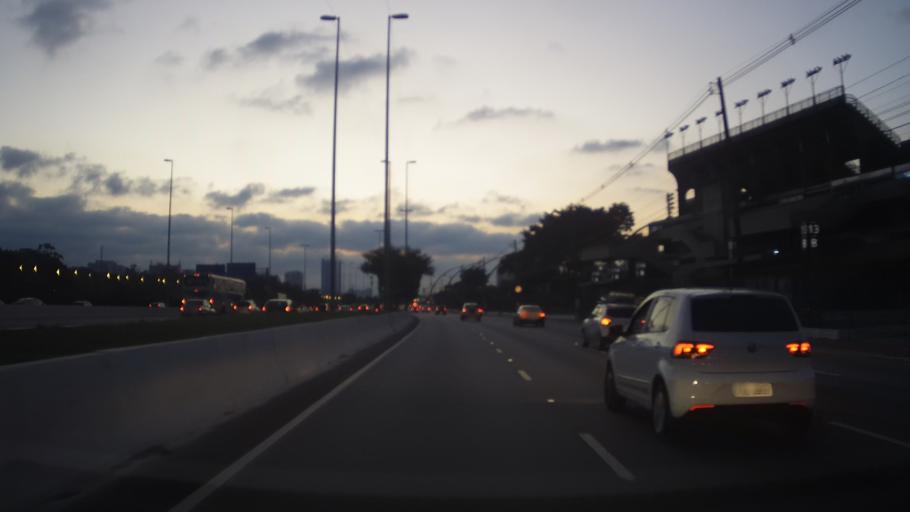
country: BR
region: Sao Paulo
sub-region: Sao Paulo
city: Sao Paulo
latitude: -23.5168
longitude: -46.6442
